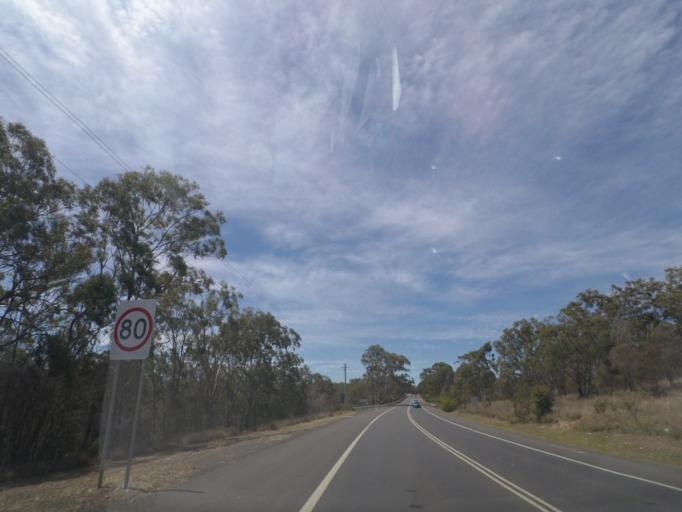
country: AU
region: New South Wales
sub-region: Wollondilly
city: Buxton
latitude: -34.2388
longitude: 150.5788
